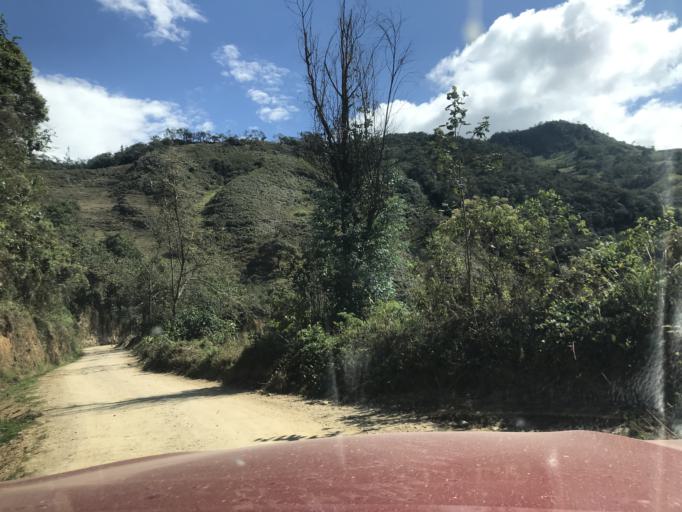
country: PE
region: Cajamarca
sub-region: Provincia de Chota
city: Querocoto
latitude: -6.3506
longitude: -79.0432
